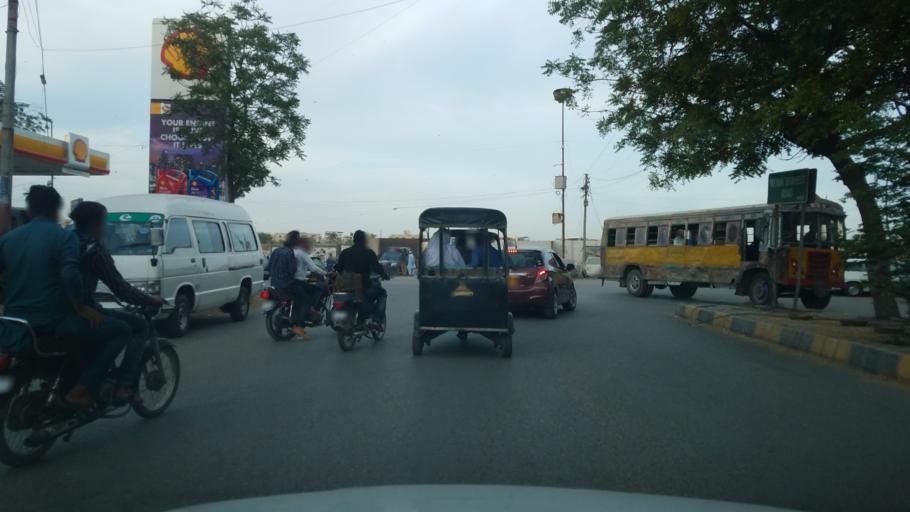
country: PK
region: Sindh
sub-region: Karachi District
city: Karachi
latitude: 24.8693
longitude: 67.0281
